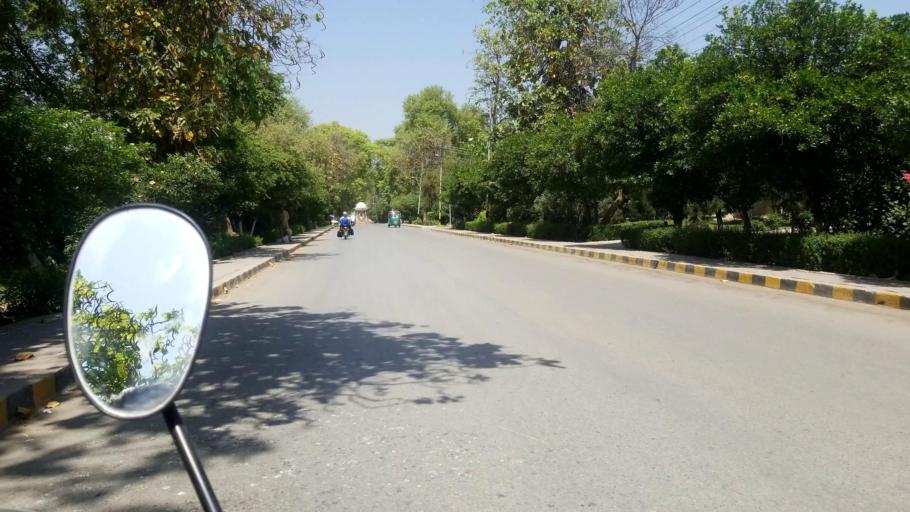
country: PK
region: Khyber Pakhtunkhwa
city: Peshawar
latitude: 34.0059
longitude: 71.4865
